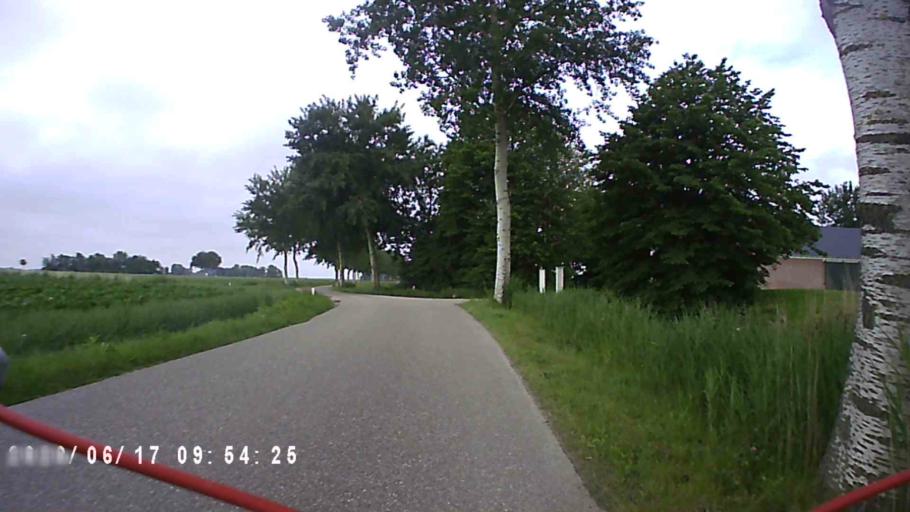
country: NL
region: Groningen
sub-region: Gemeente De Marne
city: Ulrum
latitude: 53.3599
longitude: 6.3110
